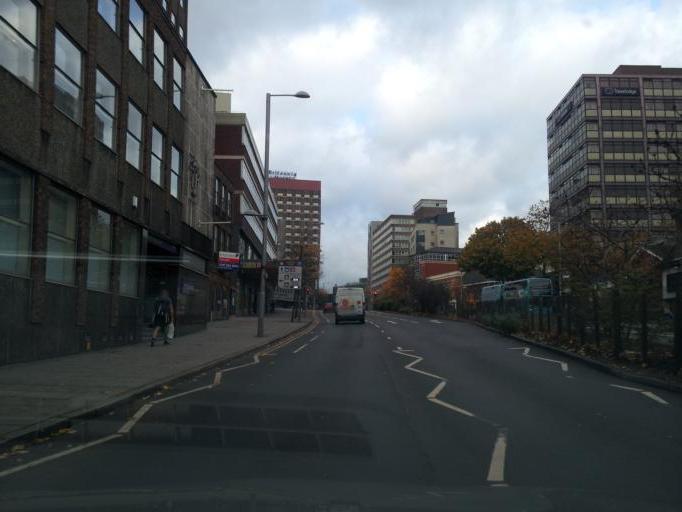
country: GB
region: England
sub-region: Nottingham
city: Nottingham
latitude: 52.9508
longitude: -1.1518
